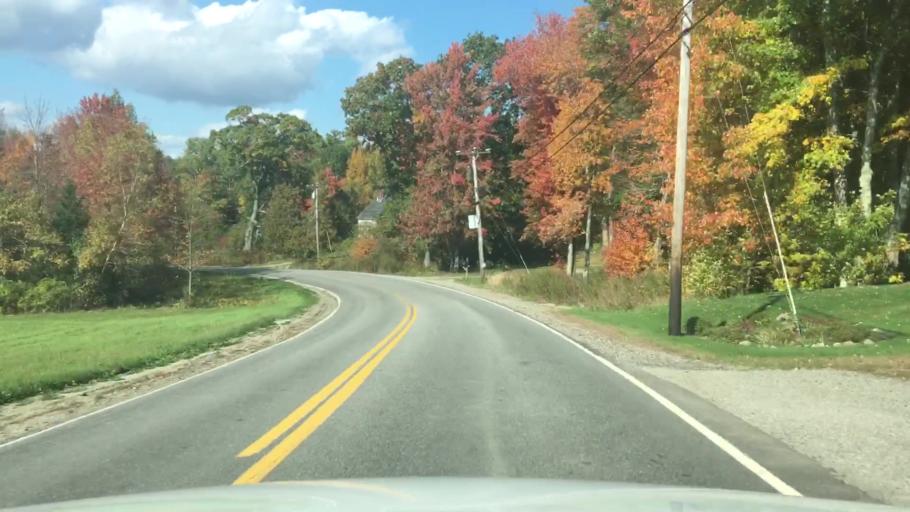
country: US
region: Maine
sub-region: Knox County
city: Warren
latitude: 44.1466
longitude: -69.2346
